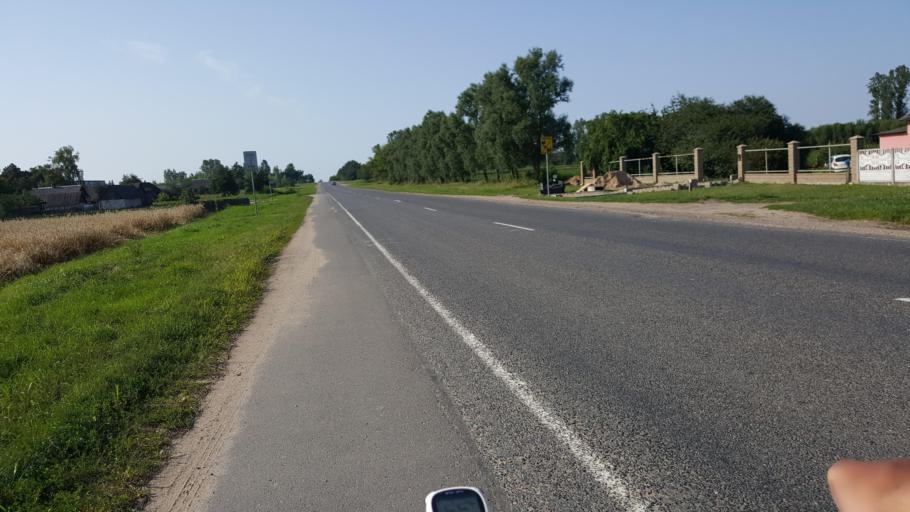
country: BY
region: Brest
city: Kamyanyets
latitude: 52.3324
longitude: 23.9131
